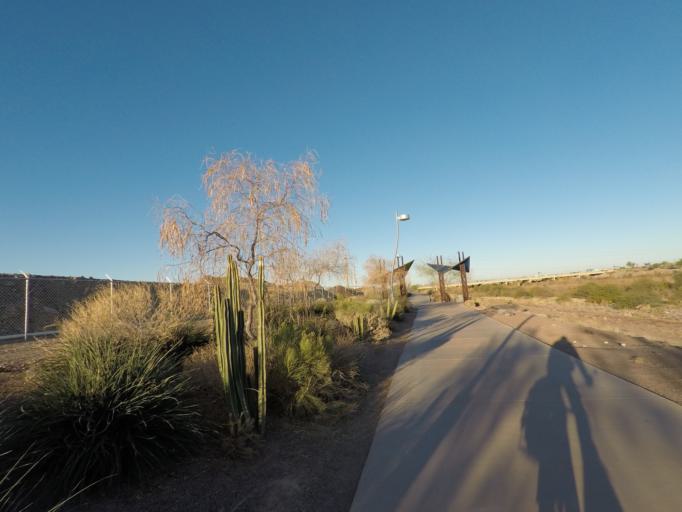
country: US
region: Arizona
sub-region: Maricopa County
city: Tempe Junction
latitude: 33.4331
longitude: -111.9549
